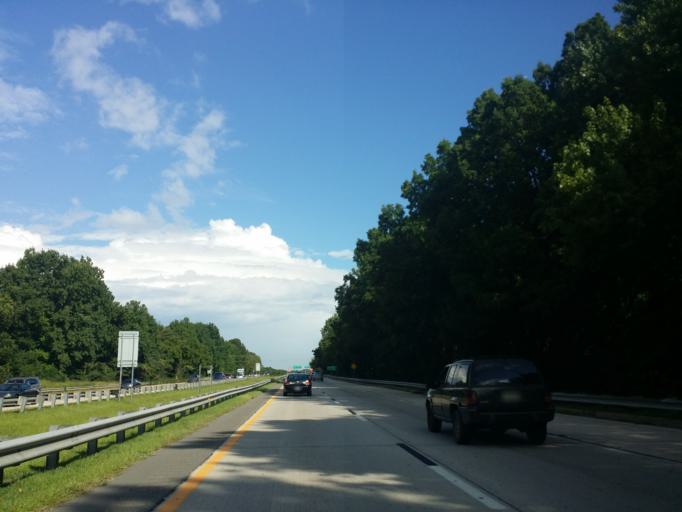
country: US
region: North Carolina
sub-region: Durham County
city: Durham
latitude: 35.9803
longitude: -78.8858
